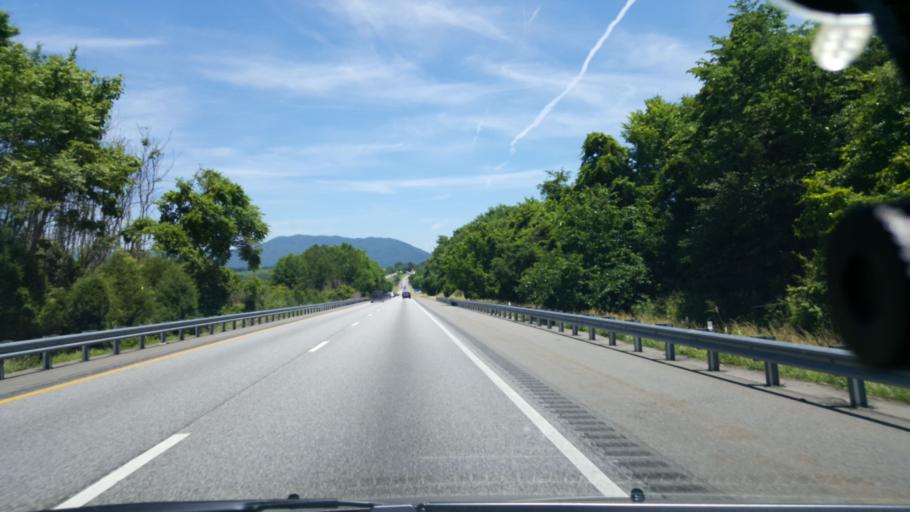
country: US
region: Virginia
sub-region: Botetourt County
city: Fincastle
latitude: 37.4843
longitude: -79.7764
